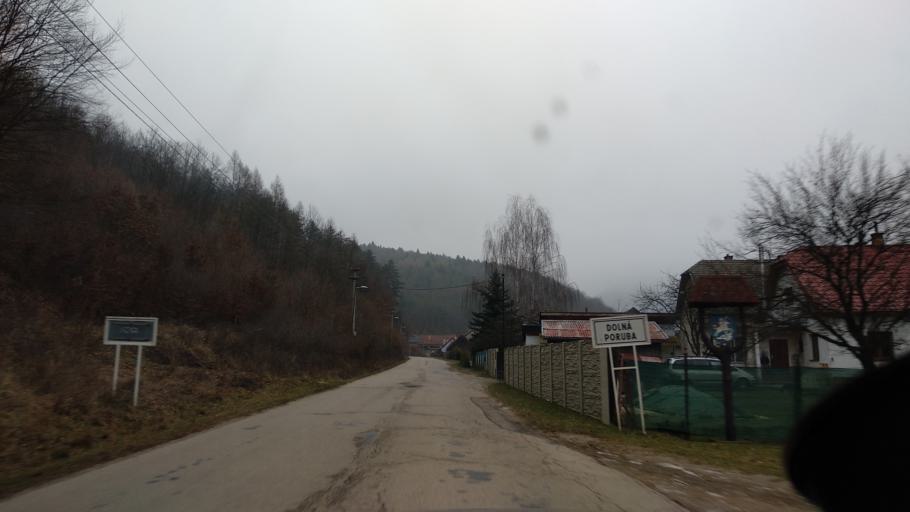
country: SK
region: Nitriansky
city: Trencianske Teplice
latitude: 48.9018
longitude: 18.2648
